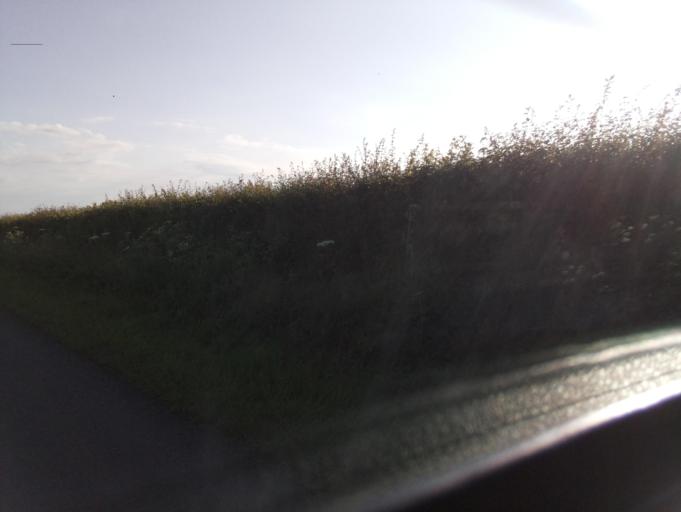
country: GB
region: England
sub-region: Lincolnshire
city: Navenby
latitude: 53.1036
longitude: -0.6077
